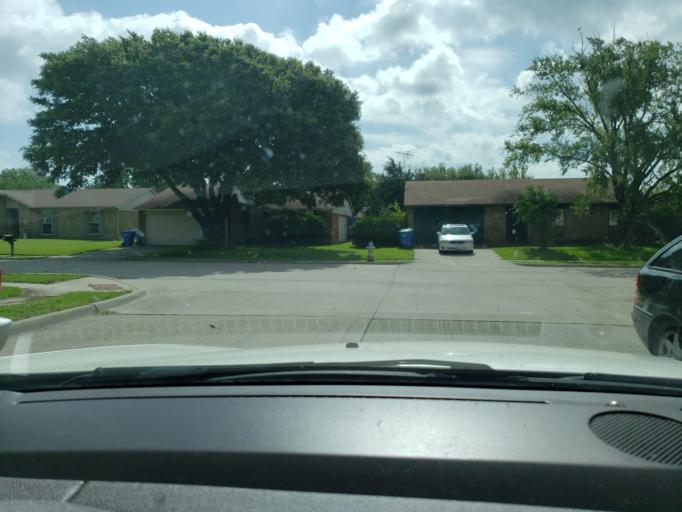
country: US
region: Texas
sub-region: Dallas County
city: Rowlett
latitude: 32.9114
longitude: -96.5713
